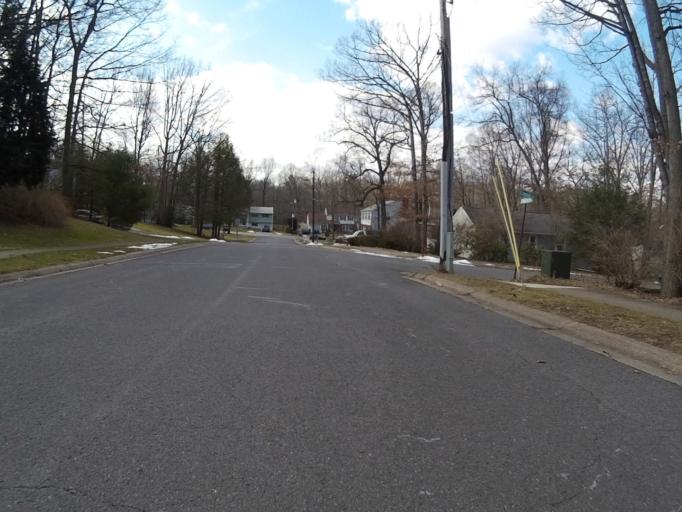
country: US
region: Pennsylvania
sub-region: Centre County
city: Park Forest Village
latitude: 40.8021
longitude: -77.9191
